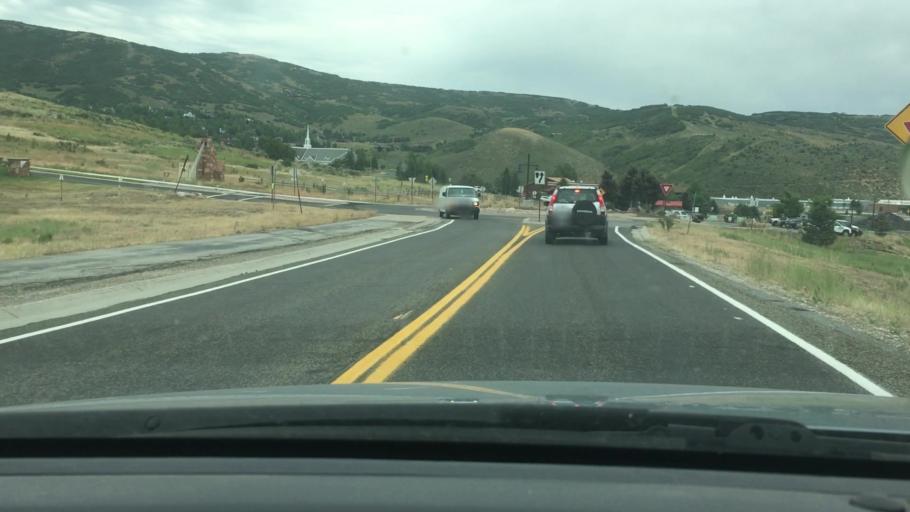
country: US
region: Utah
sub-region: Summit County
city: Summit Park
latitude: 40.7557
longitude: -111.5744
